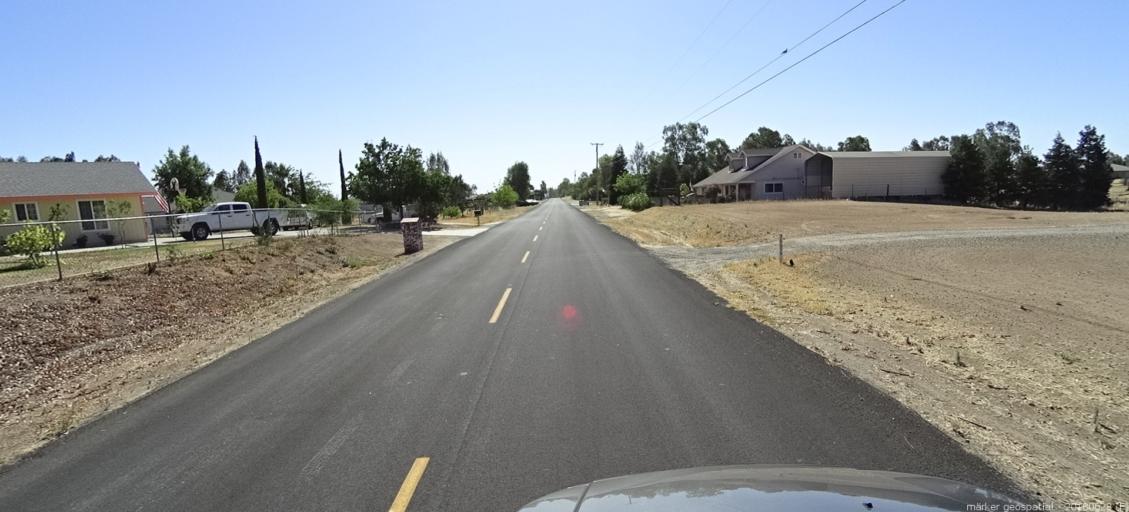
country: US
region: California
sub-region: Madera County
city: Bonadelle Ranchos-Madera Ranchos
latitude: 37.0085
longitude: -119.8820
